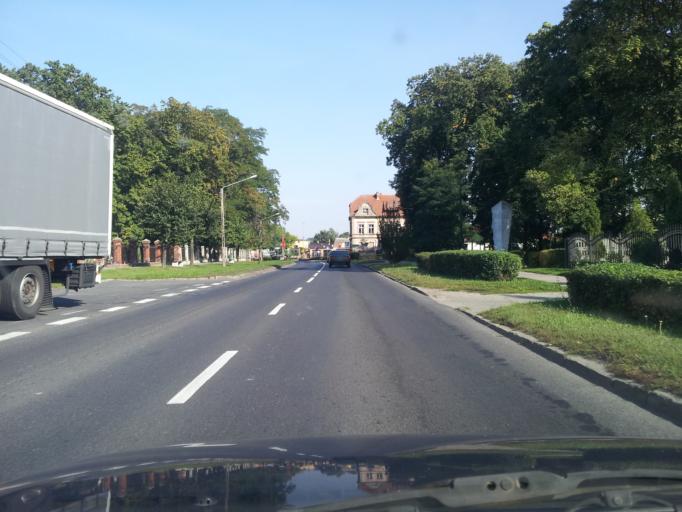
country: PL
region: Kujawsko-Pomorskie
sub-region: Powiat mogilenski
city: Strzelno
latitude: 52.6274
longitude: 18.1671
